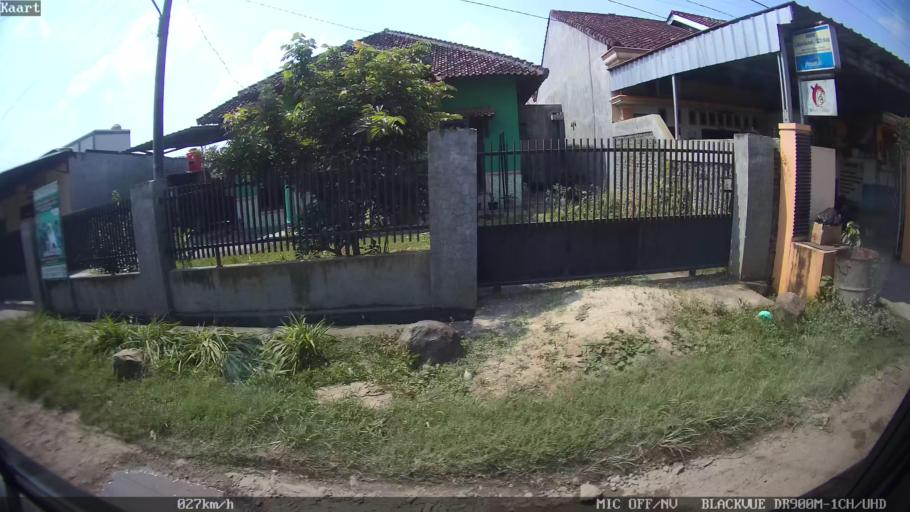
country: ID
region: Lampung
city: Natar
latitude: -5.3096
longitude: 105.2104
